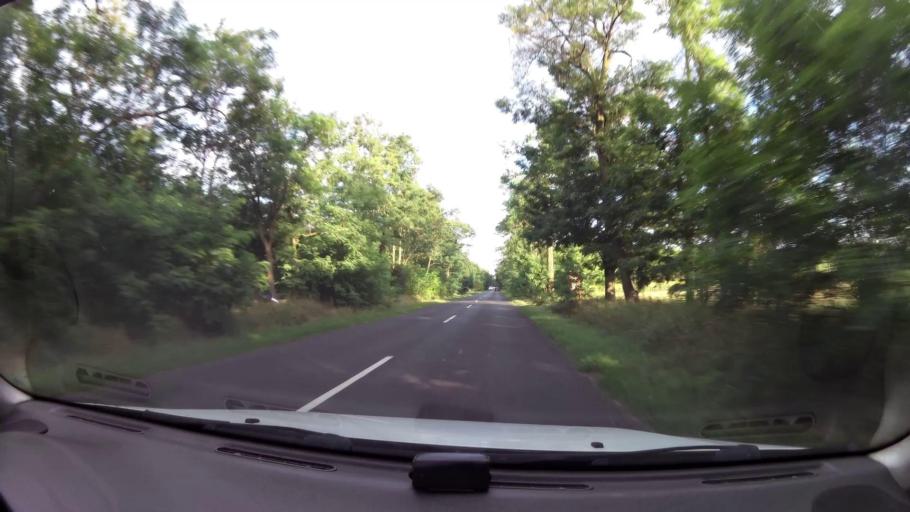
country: HU
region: Pest
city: Tapioszecso
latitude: 47.4301
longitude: 19.6032
